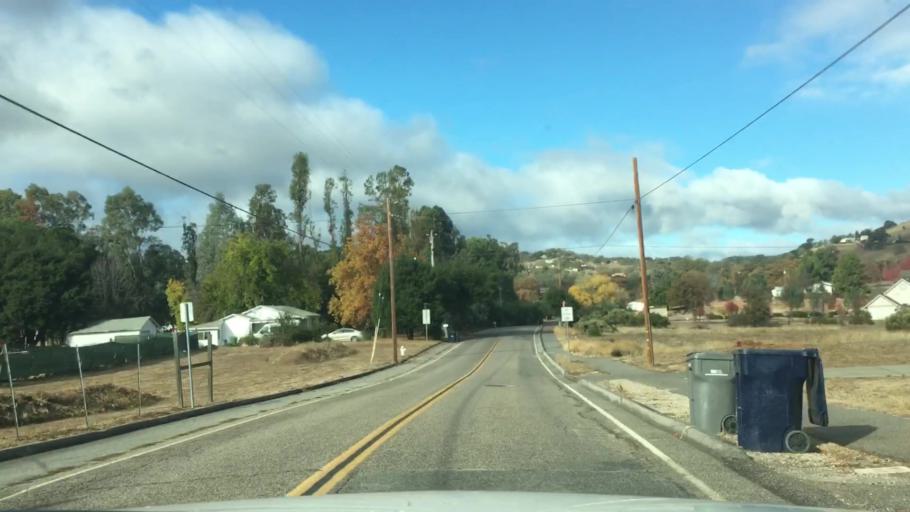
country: US
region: California
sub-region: San Luis Obispo County
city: Atascadero
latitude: 35.4597
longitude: -120.6701
